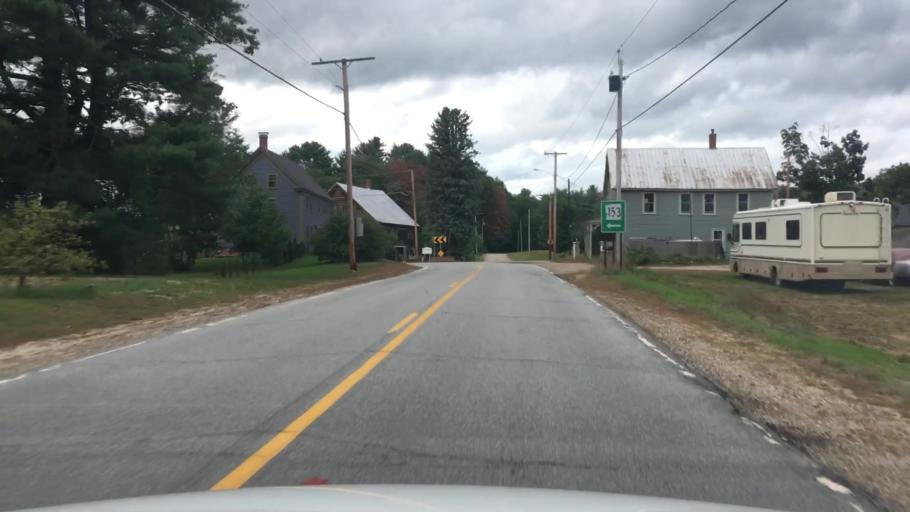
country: US
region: New Hampshire
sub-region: Carroll County
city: Effingham
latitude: 43.7113
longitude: -70.9820
